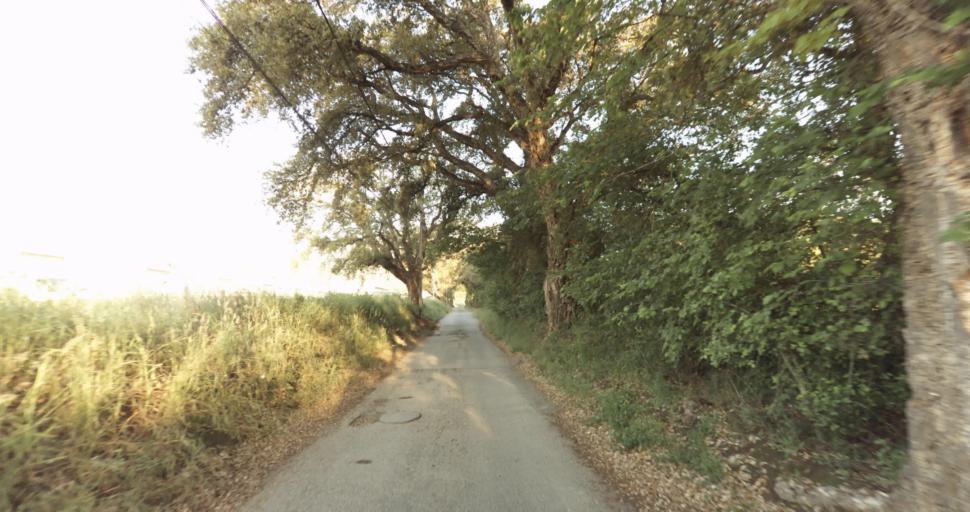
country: FR
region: Corsica
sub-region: Departement de la Haute-Corse
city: Biguglia
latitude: 42.6288
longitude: 9.4438
